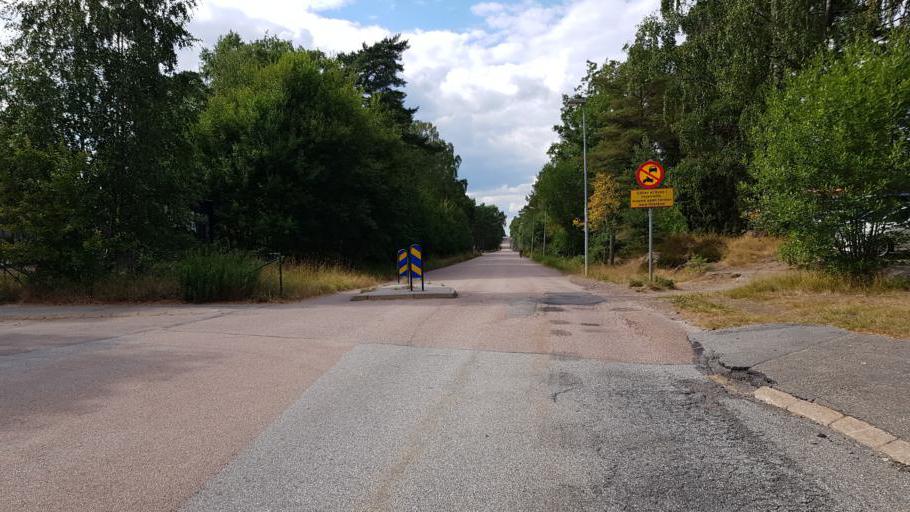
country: SE
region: Vaestra Goetaland
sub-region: Partille Kommun
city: Furulund
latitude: 57.7114
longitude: 12.1448
